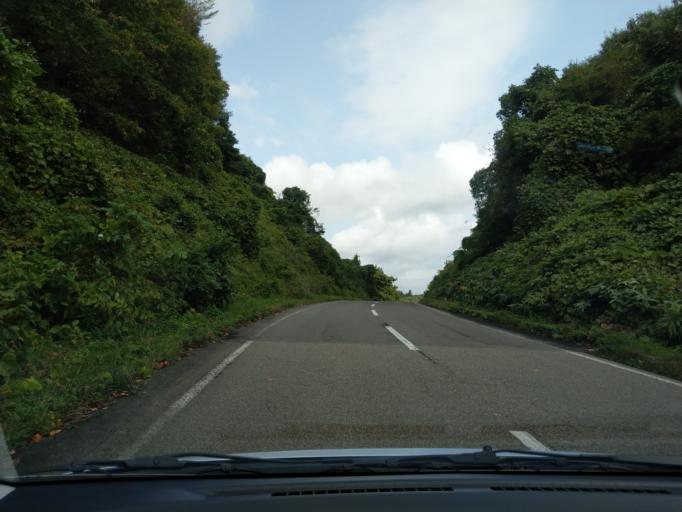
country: JP
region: Akita
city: Omagari
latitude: 39.4765
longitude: 140.3090
